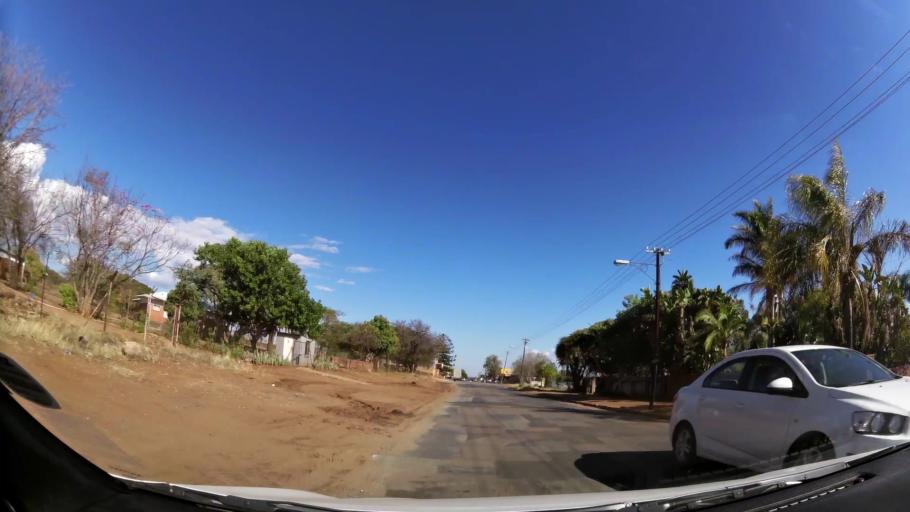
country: ZA
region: Limpopo
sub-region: Waterberg District Municipality
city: Mokopane
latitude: -24.1781
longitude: 29.0171
